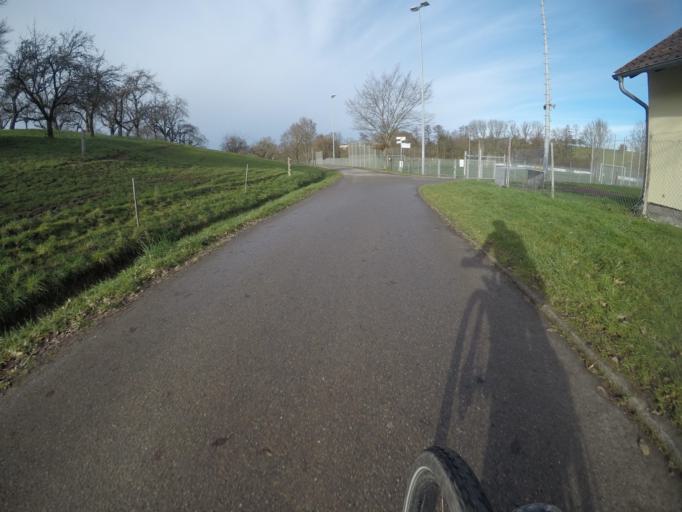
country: DE
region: Baden-Wuerttemberg
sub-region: Regierungsbezirk Stuttgart
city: Leutenbach
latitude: 48.8916
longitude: 9.3809
